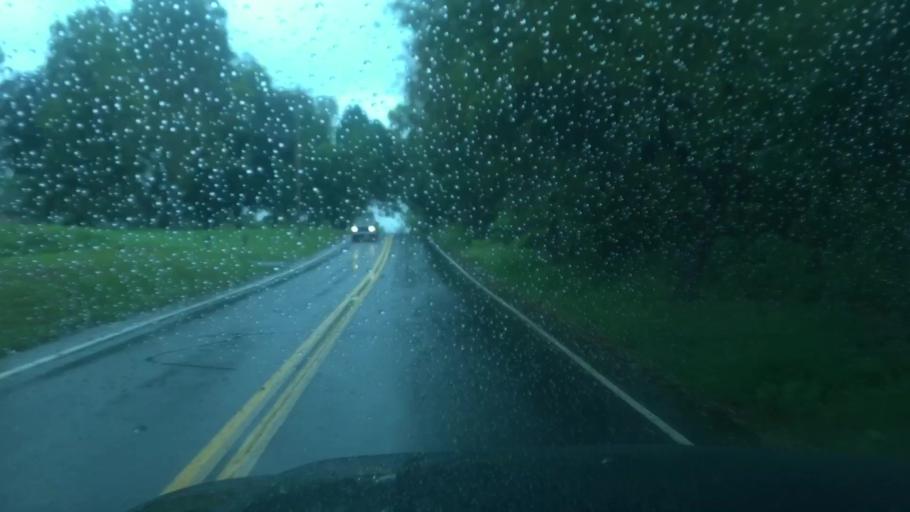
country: US
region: Pennsylvania
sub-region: Cumberland County
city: Shiremanstown
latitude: 40.1716
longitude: -76.9640
